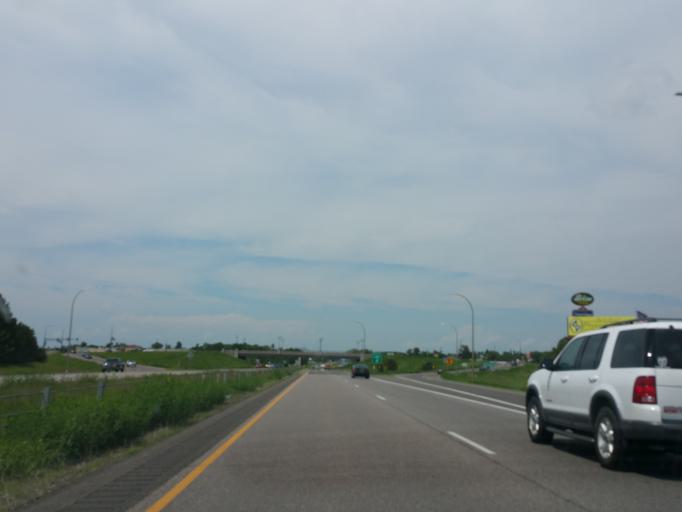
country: US
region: Minnesota
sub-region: Chisago County
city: North Branch
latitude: 45.5068
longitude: -92.9932
